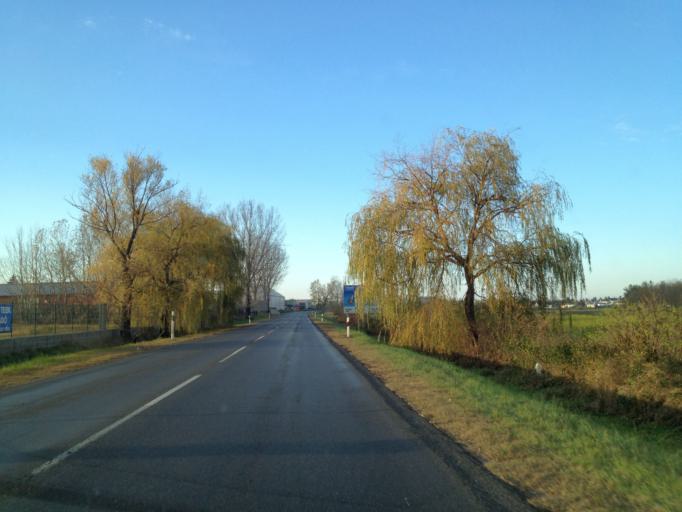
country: HU
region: Gyor-Moson-Sopron
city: Gyorujbarat
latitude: 47.6447
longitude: 17.6614
